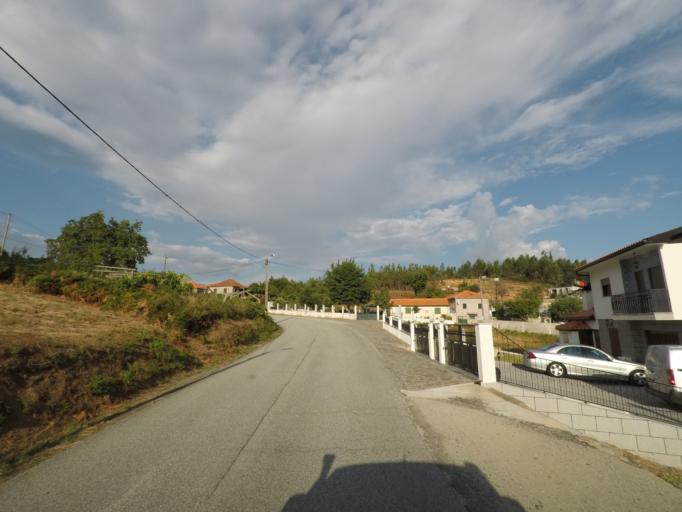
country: PT
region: Porto
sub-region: Baiao
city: Valadares
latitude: 41.1778
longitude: -7.9358
